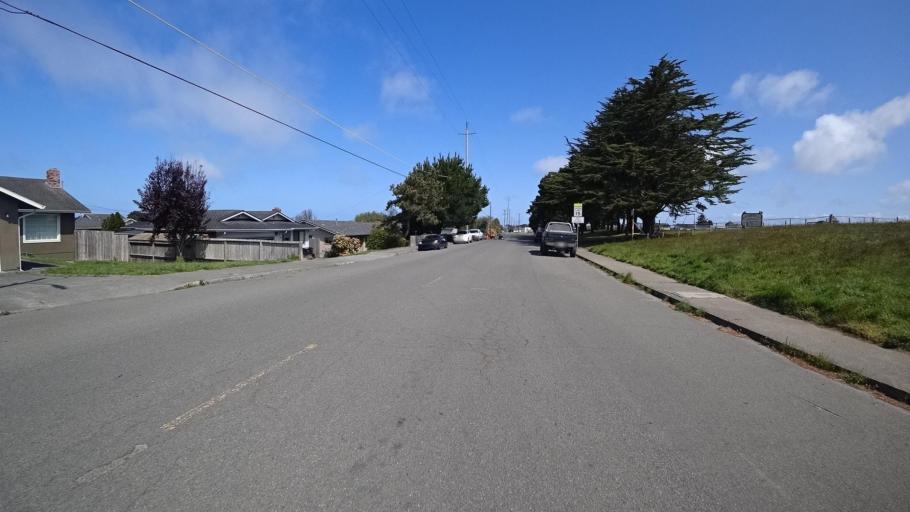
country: US
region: California
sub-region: Humboldt County
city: Bayview
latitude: 40.7746
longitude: -124.1801
